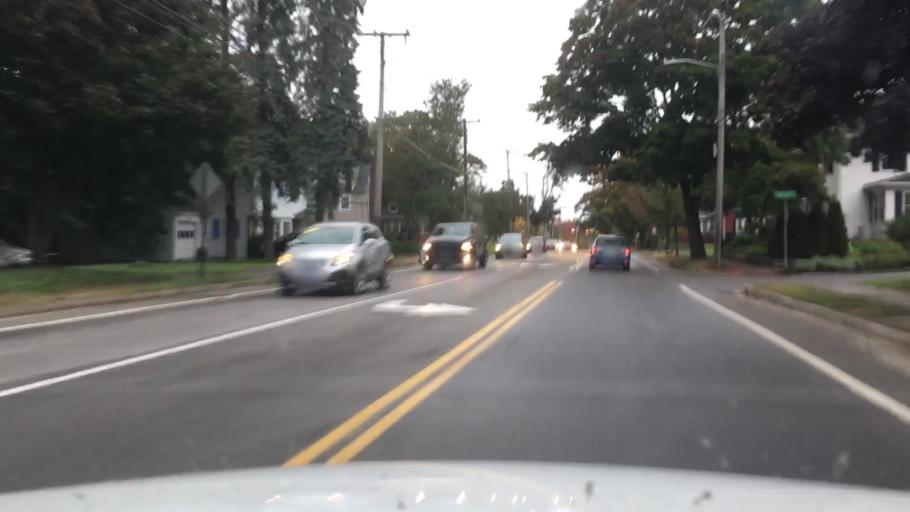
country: US
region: Maine
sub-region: Cumberland County
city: South Portland Gardens
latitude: 43.6658
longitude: -70.2928
